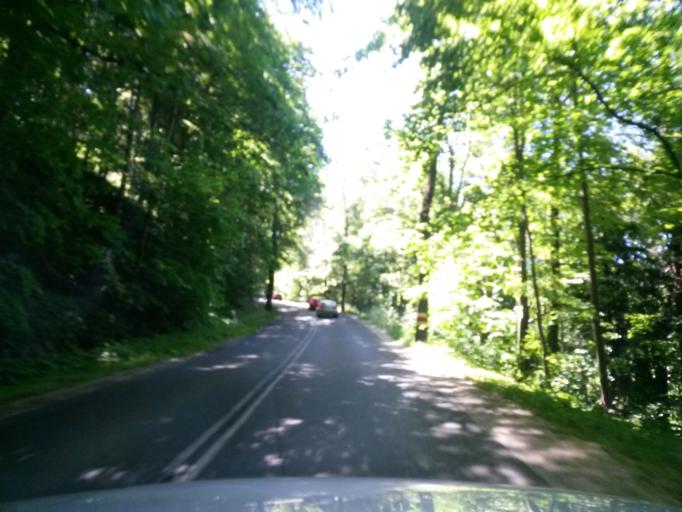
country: PL
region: Lower Silesian Voivodeship
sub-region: Powiat jeleniogorski
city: Kowary
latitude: 50.7717
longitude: 15.8567
